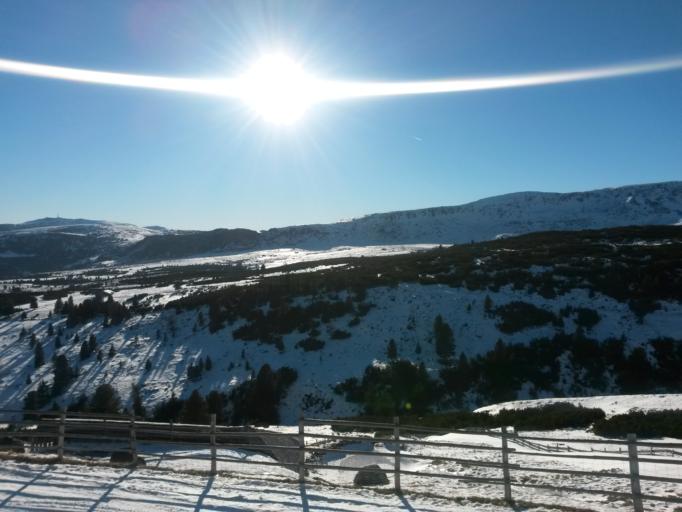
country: IT
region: Trentino-Alto Adige
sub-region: Bolzano
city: Villandro - Villanders
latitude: 46.6695
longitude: 11.4747
